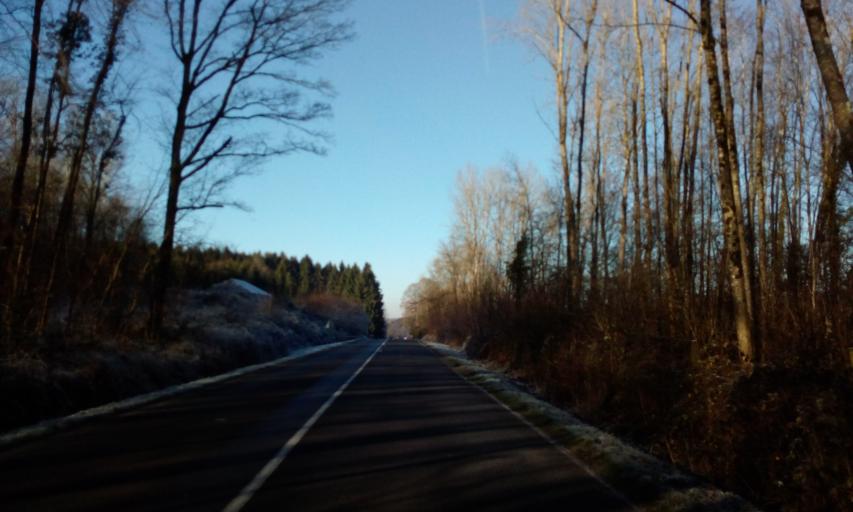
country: FR
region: Champagne-Ardenne
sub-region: Departement des Ardennes
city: Rimogne
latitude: 49.8264
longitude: 4.5065
